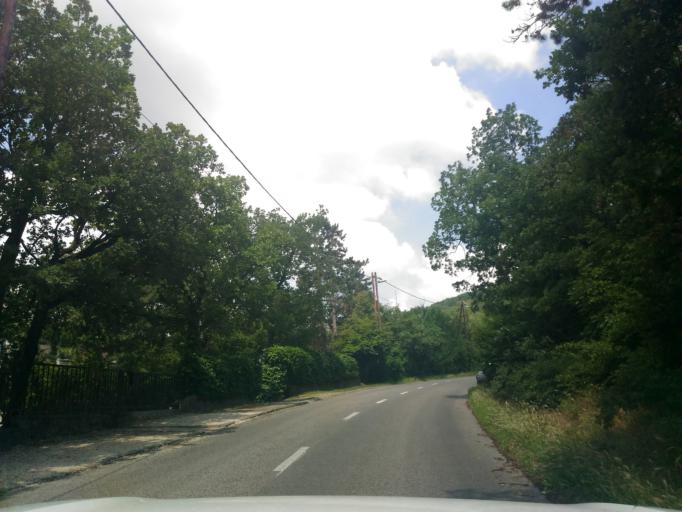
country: HU
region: Baranya
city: Pecs
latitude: 46.0925
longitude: 18.2269
